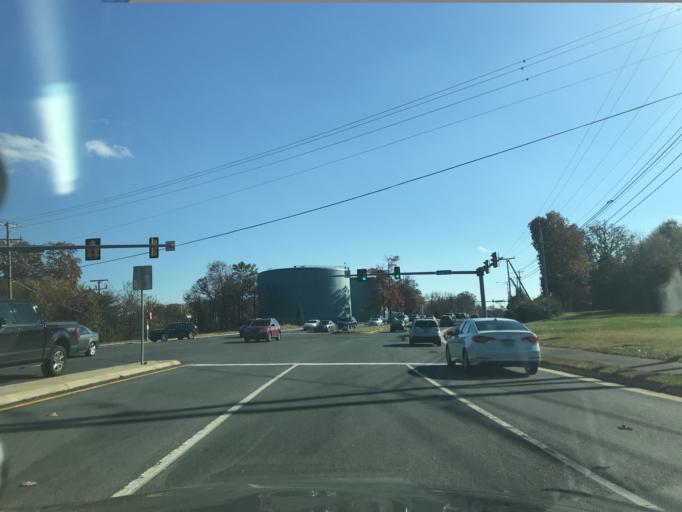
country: US
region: Virginia
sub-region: Fairfax County
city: Greenbriar
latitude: 38.8813
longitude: -77.3695
